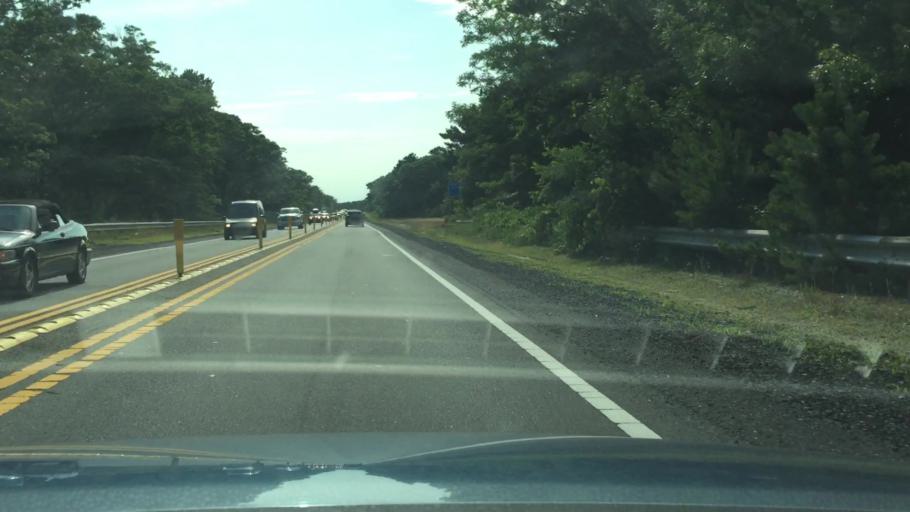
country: US
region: Massachusetts
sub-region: Barnstable County
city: South Dennis
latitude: 41.7004
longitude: -70.1328
